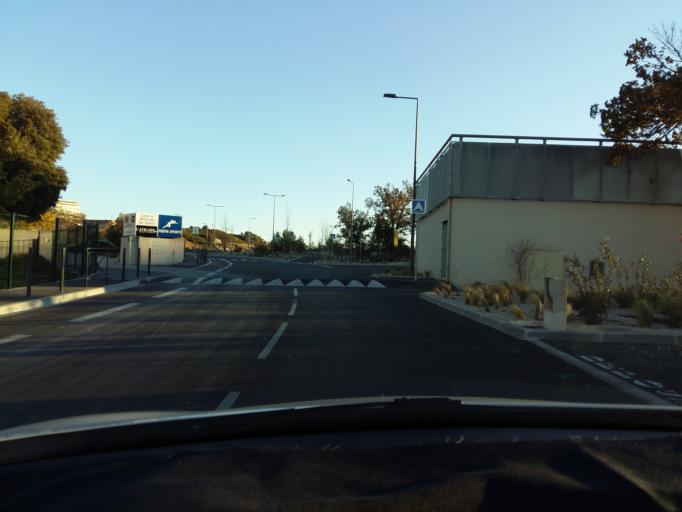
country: FR
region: Provence-Alpes-Cote d'Azur
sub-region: Departement des Bouches-du-Rhone
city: Cabries
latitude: 43.4898
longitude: 5.3518
